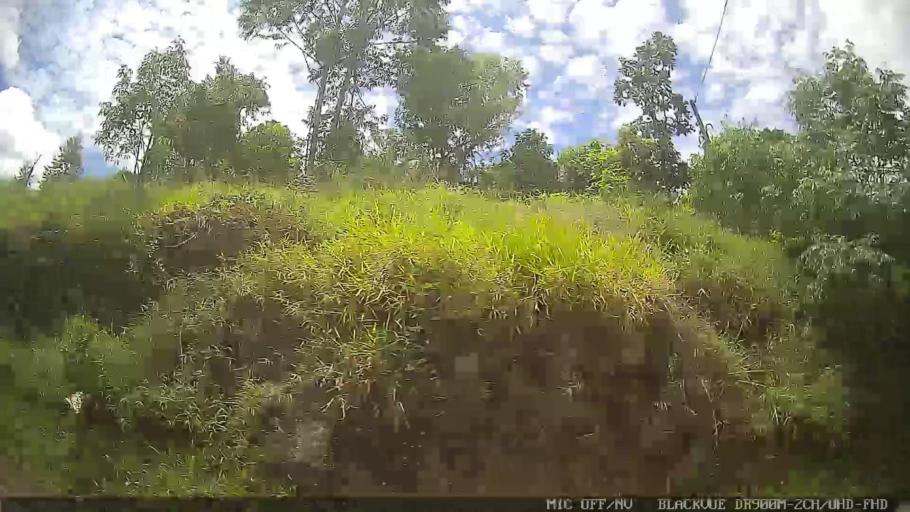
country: BR
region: Sao Paulo
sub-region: Biritiba-Mirim
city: Biritiba Mirim
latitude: -23.5665
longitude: -46.0246
